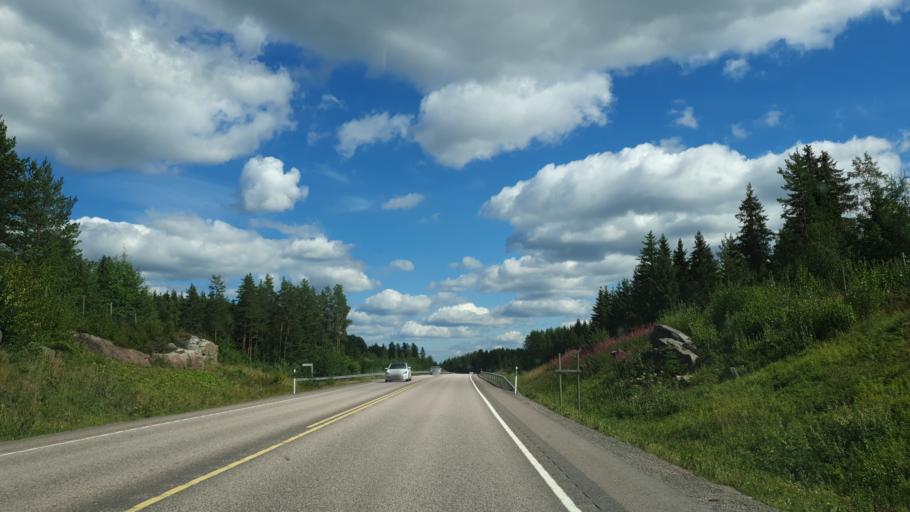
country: FI
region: Pirkanmaa
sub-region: Tampere
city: Kuhmalahti
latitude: 61.7093
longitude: 24.6109
